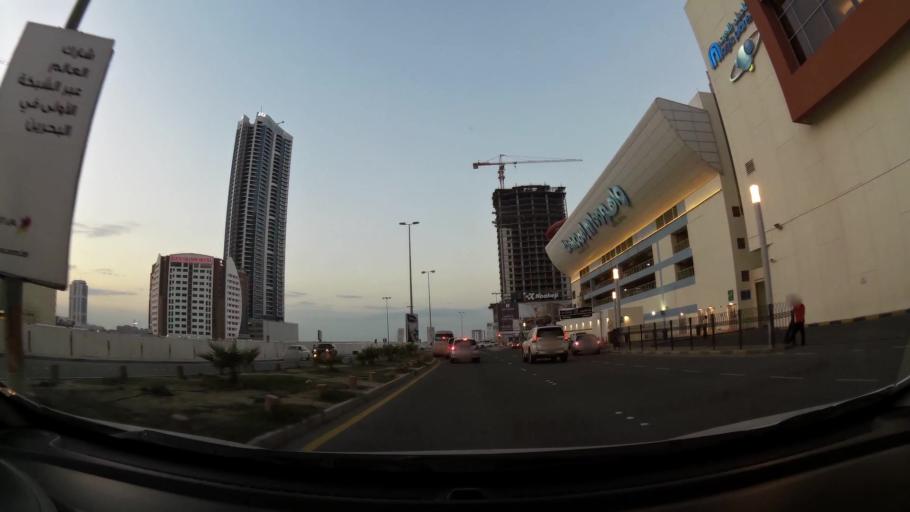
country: BH
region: Manama
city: Jidd Hafs
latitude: 26.2336
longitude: 50.5515
